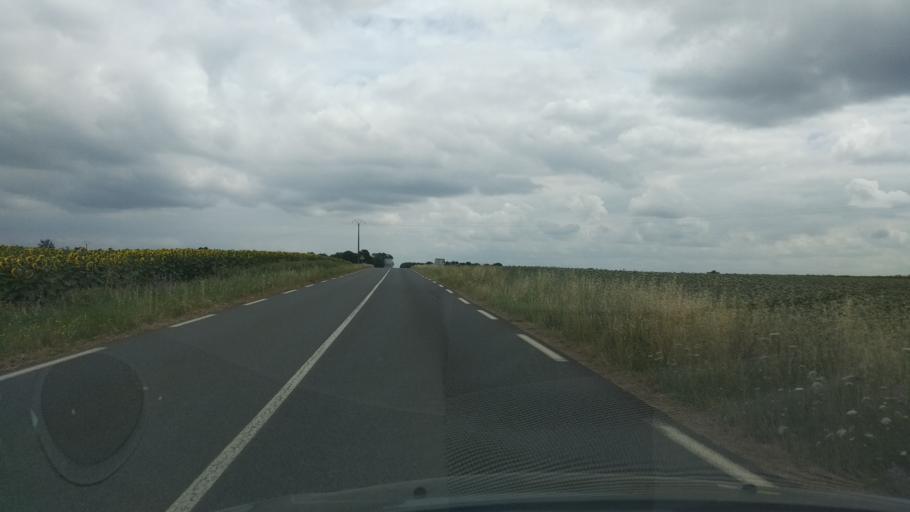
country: FR
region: Poitou-Charentes
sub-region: Departement de la Vienne
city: La Villedieu-du-Clain
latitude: 46.4385
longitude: 0.3714
